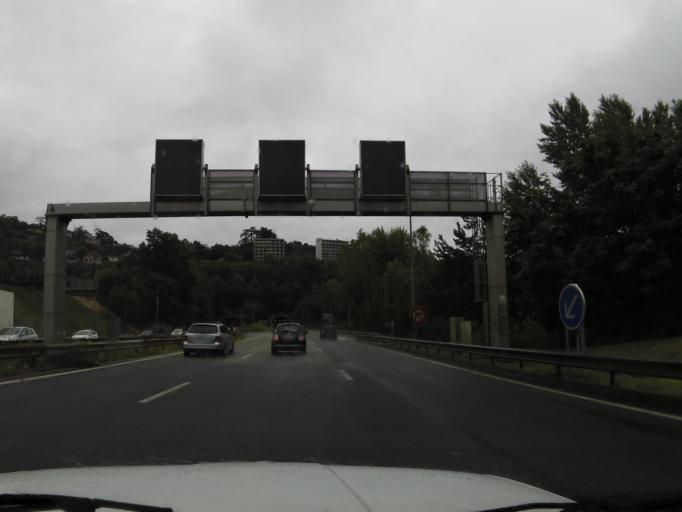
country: FR
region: Rhone-Alpes
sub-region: Departement de la Savoie
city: Chambery
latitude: 45.5777
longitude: 5.9195
